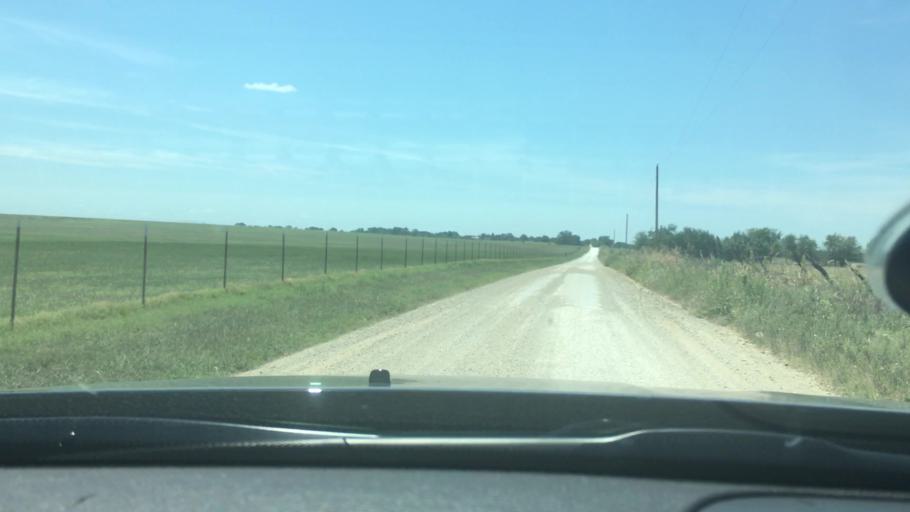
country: US
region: Oklahoma
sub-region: Bryan County
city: Durant
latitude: 34.0086
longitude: -96.1123
